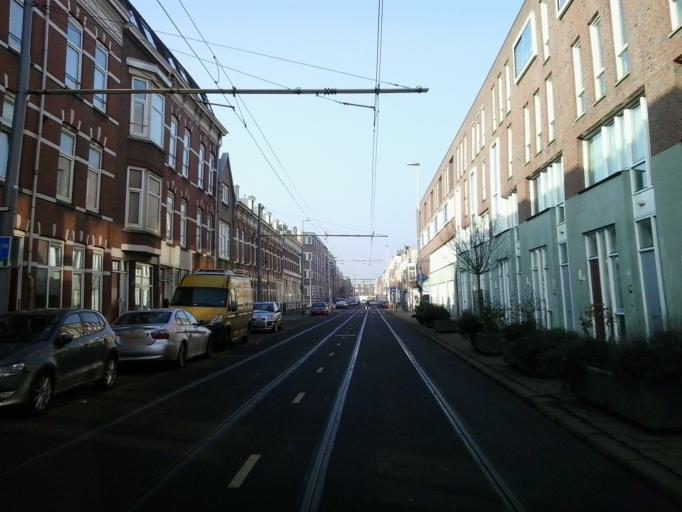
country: NL
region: South Holland
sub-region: Gemeente Rotterdam
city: Rotterdam
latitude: 51.9346
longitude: 4.4832
